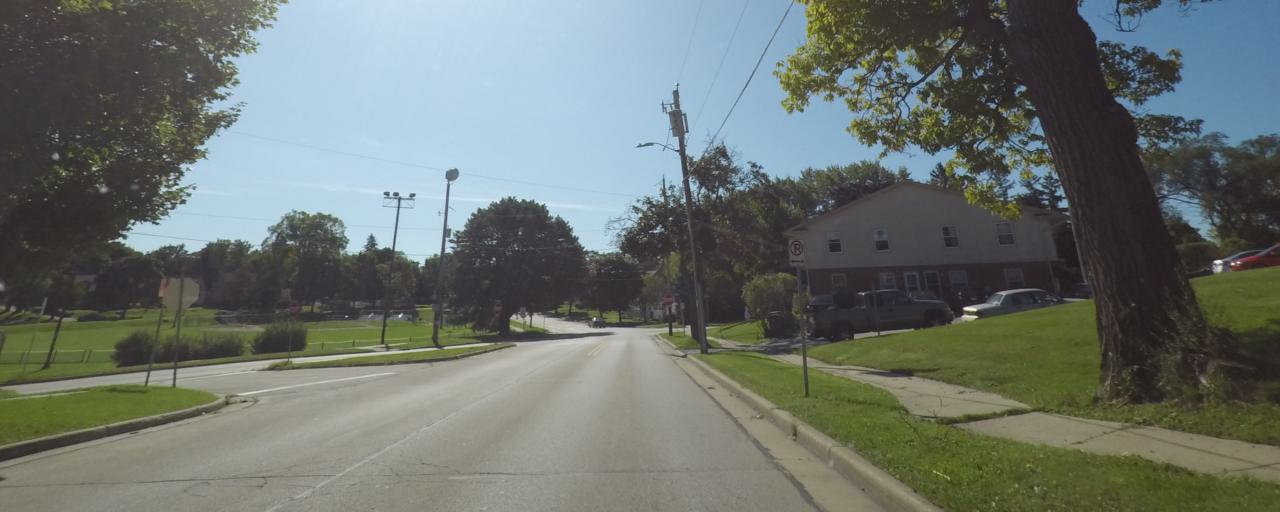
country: US
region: Wisconsin
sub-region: Waukesha County
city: Waukesha
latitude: 43.0037
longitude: -88.2173
